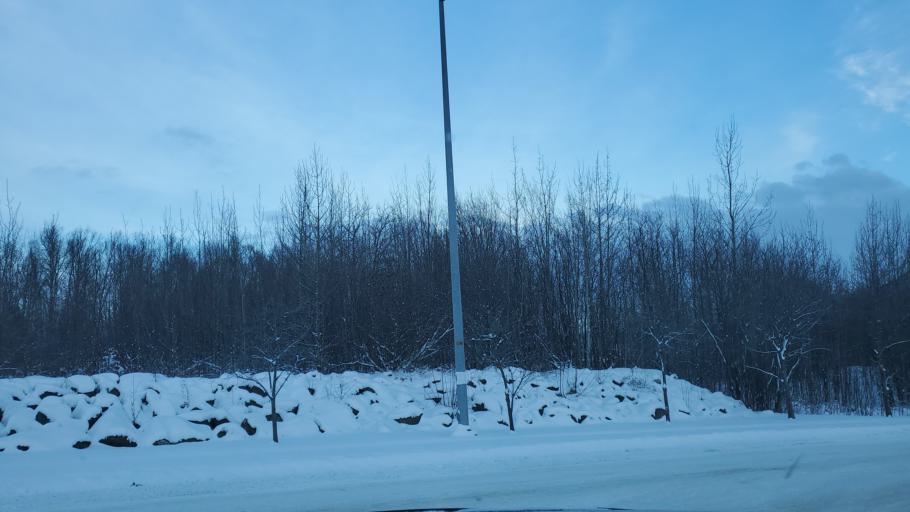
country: US
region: Alaska
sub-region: Matanuska-Susitna Borough
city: Palmer
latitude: 61.5942
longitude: -149.1203
